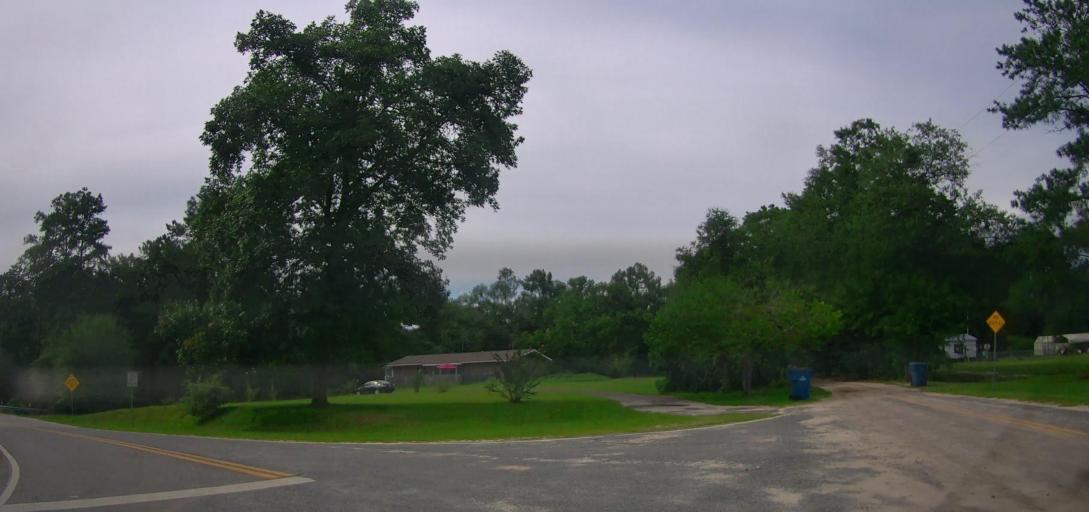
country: US
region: Georgia
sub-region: Wayne County
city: Jesup
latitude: 31.6764
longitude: -81.9068
